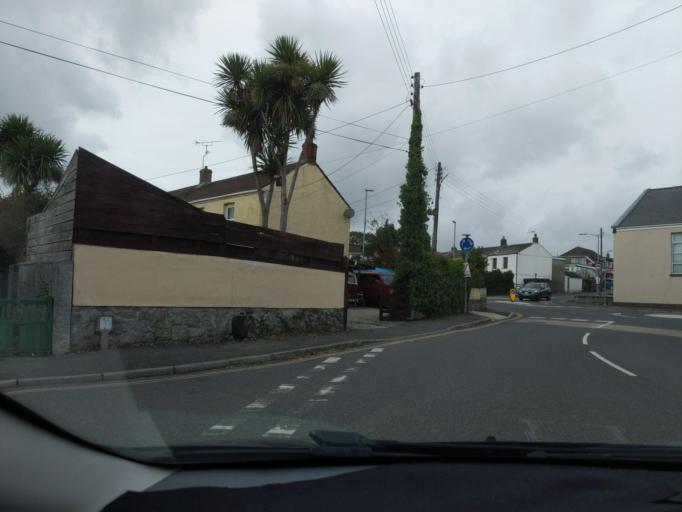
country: GB
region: England
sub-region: Cornwall
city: St Austell
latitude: 50.3438
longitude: -4.7635
